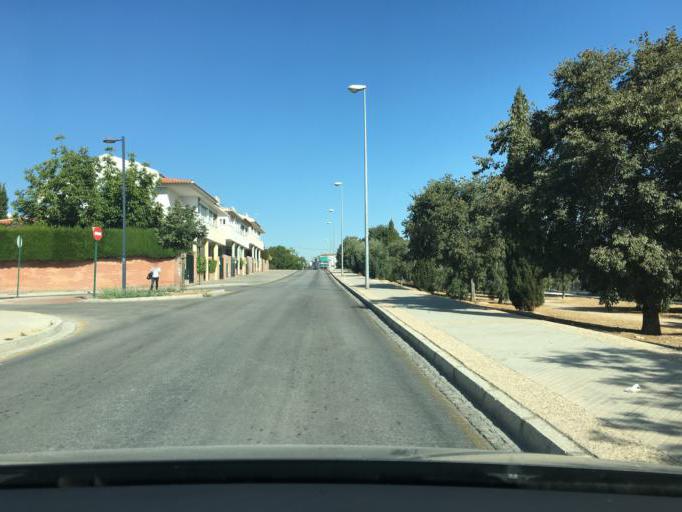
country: ES
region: Andalusia
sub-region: Provincia de Granada
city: Maracena
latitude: 37.1981
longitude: -3.6233
